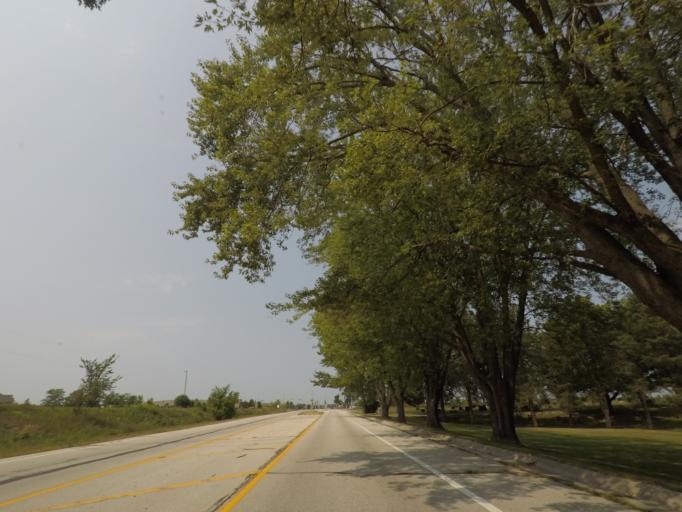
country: US
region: Wisconsin
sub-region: Waukesha County
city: Dousman
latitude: 43.0620
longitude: -88.4653
